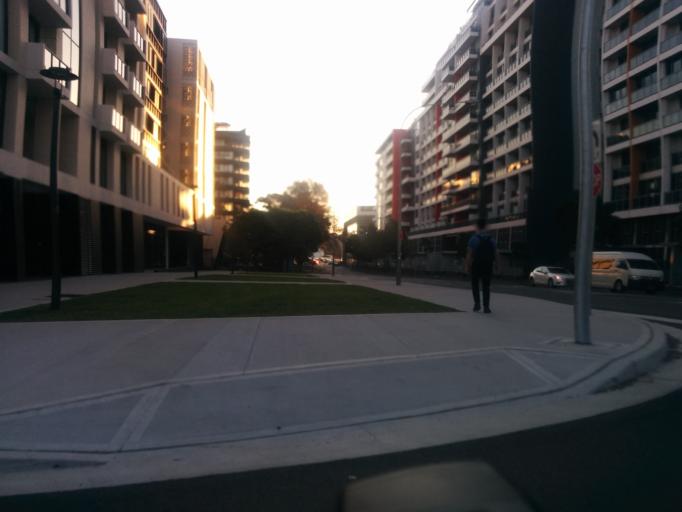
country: AU
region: New South Wales
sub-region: City of Sydney
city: Redfern
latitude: -33.9007
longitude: 151.2131
